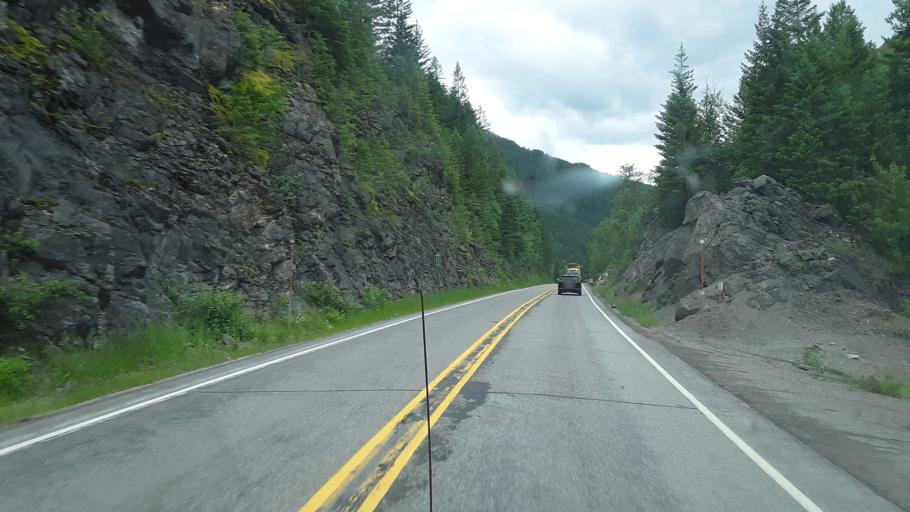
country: US
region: Montana
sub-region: Flathead County
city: Columbia Falls
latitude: 48.4935
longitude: -113.8963
